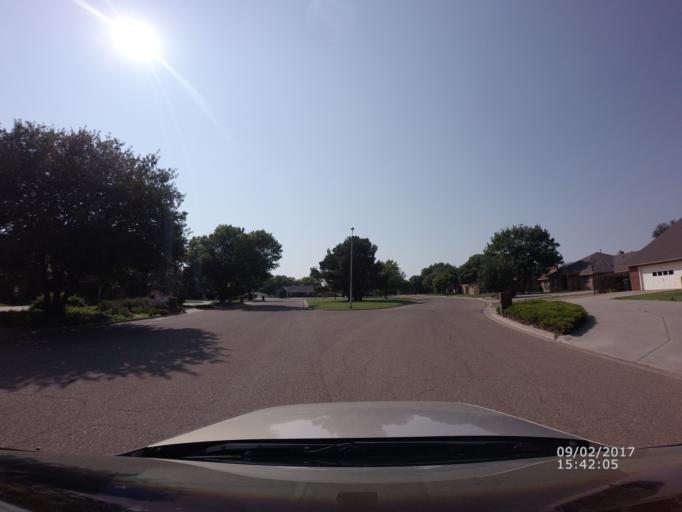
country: US
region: New Mexico
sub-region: Curry County
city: Clovis
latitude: 34.4443
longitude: -103.1925
